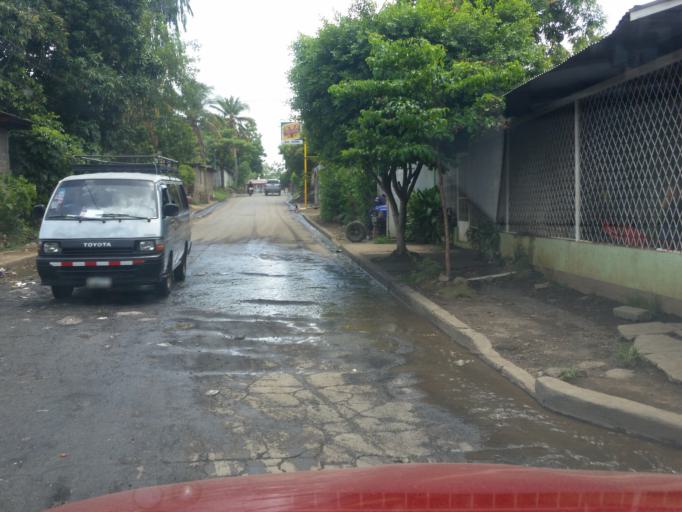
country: NI
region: Managua
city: Managua
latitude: 12.1057
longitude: -86.2320
